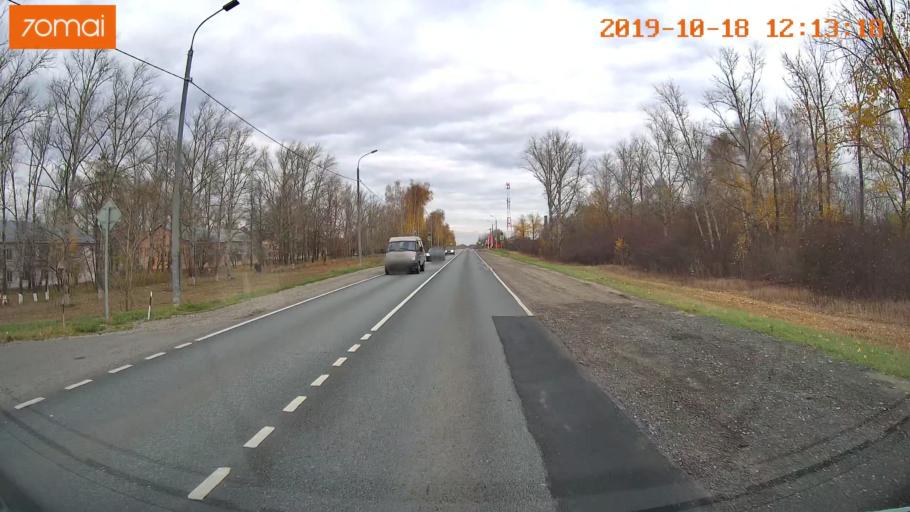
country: RU
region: Rjazan
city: Zakharovo
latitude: 54.4200
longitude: 39.3687
